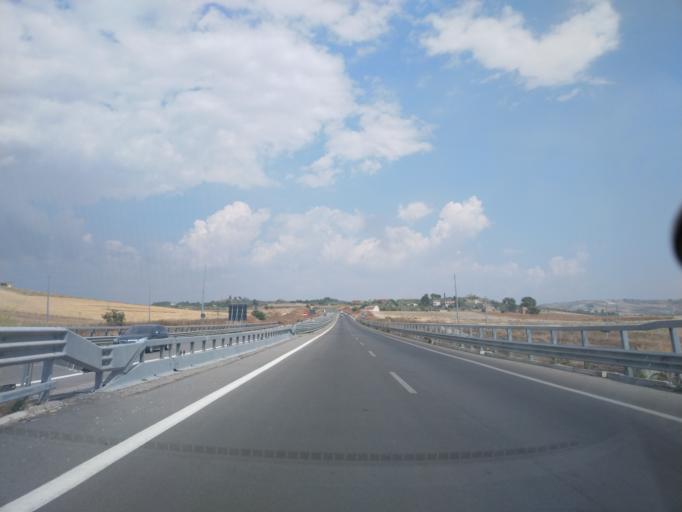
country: IT
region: Sicily
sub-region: Agrigento
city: Grotte
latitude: 37.3596
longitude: 13.6889
